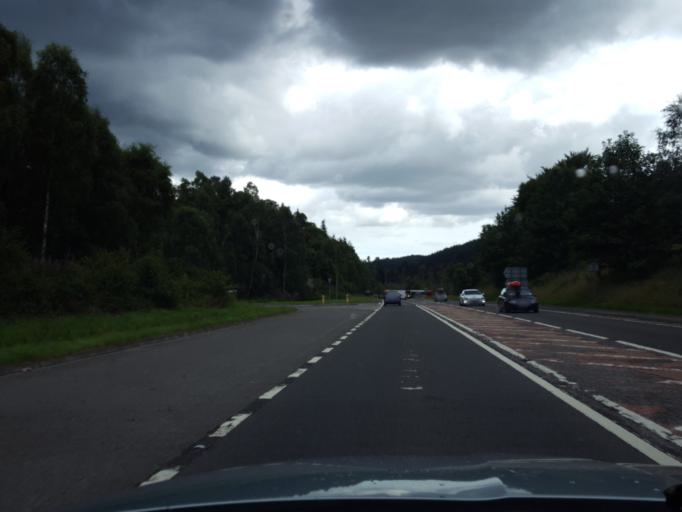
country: GB
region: Scotland
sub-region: Perth and Kinross
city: Bankfoot
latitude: 56.5522
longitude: -3.5648
